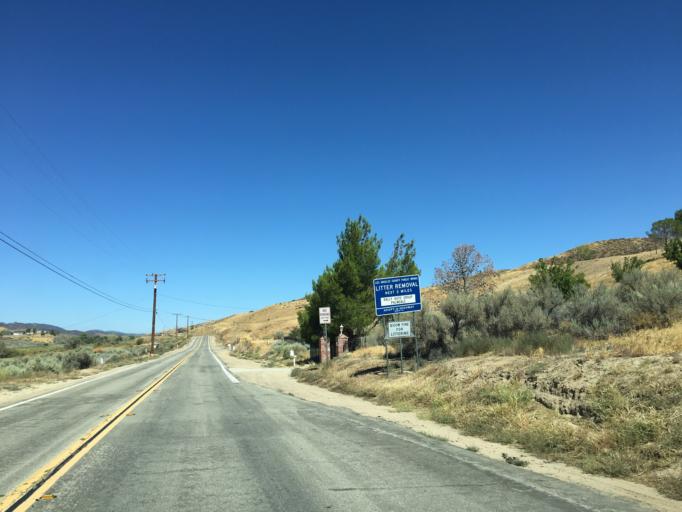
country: US
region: California
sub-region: Los Angeles County
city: Leona Valley
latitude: 34.6240
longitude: -118.3045
